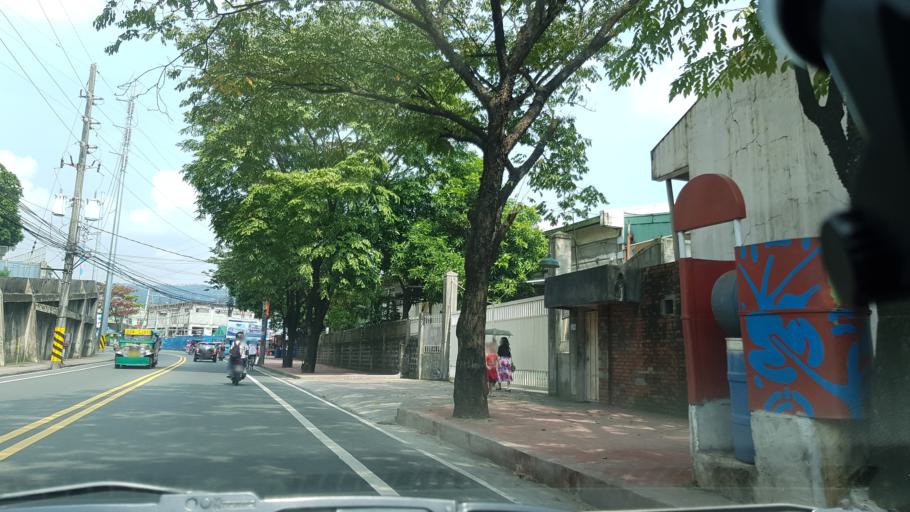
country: PH
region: Calabarzon
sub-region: Province of Rizal
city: San Mateo
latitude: 14.6633
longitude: 121.1249
